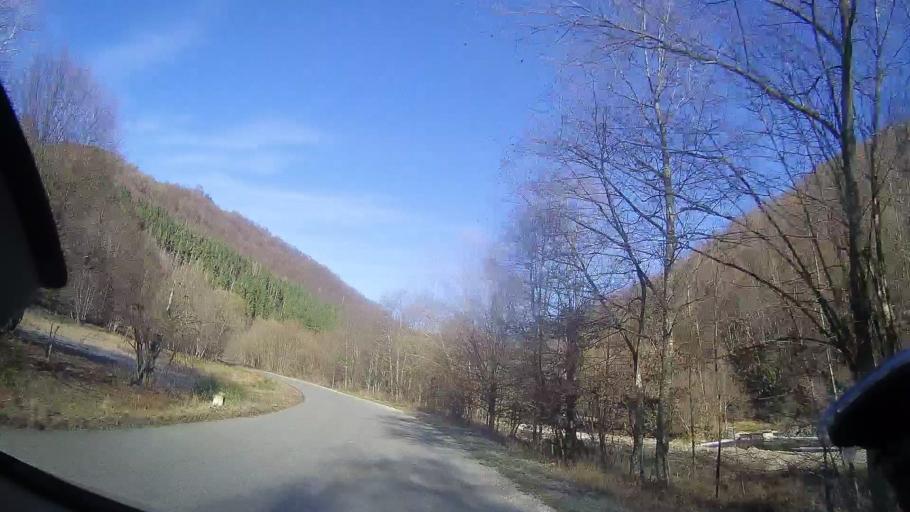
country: RO
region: Cluj
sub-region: Comuna Sacueu
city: Sacuieu
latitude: 46.8492
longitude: 22.8629
